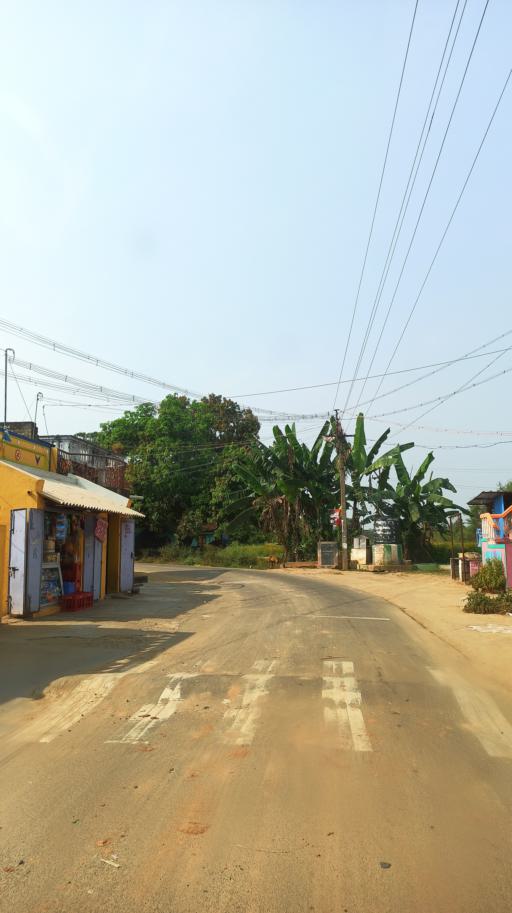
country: IN
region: Tamil Nadu
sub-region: Tiruvannamalai
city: Desur
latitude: 12.4542
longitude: 79.3729
